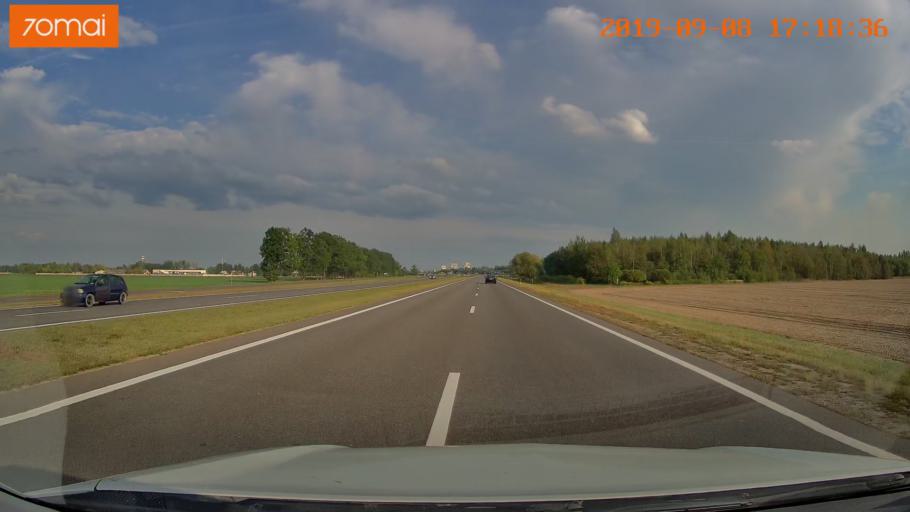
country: BY
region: Grodnenskaya
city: Skidal'
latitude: 53.5858
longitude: 24.1756
